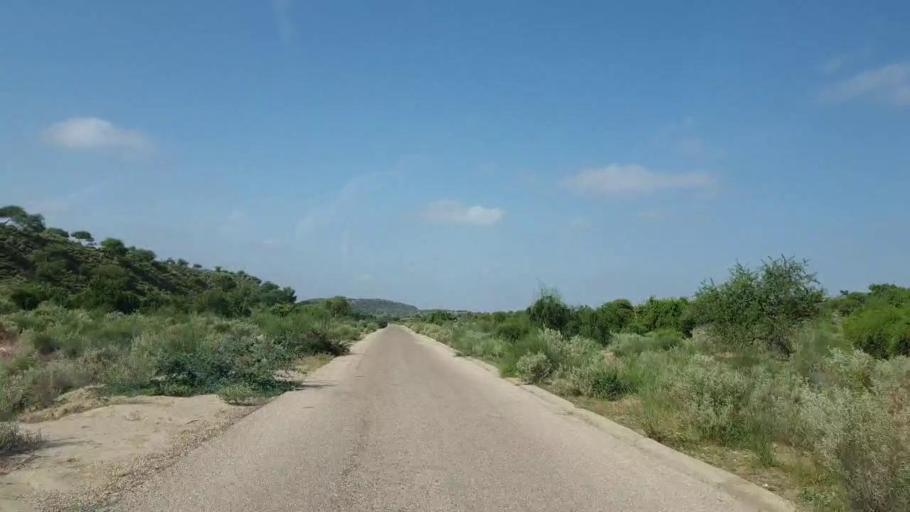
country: PK
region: Sindh
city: Mithi
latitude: 24.5592
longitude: 69.9003
